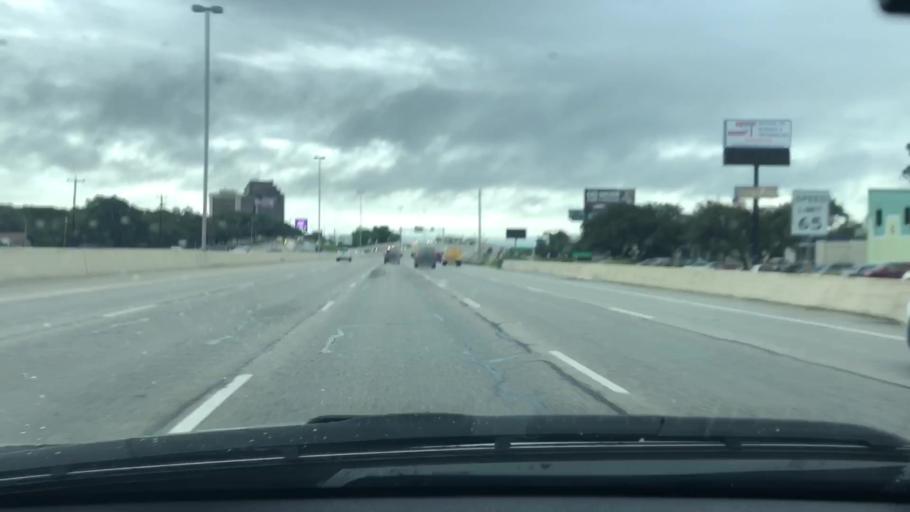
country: US
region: Texas
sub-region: Bexar County
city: Alamo Heights
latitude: 29.5160
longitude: -98.4452
